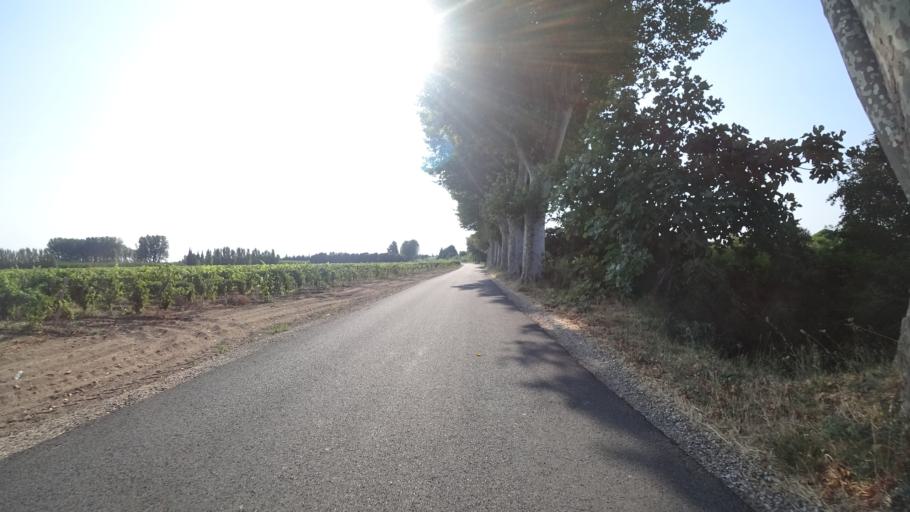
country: FR
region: Languedoc-Roussillon
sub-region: Departement des Pyrenees-Orientales
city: Claira
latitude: 42.7591
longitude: 2.9663
